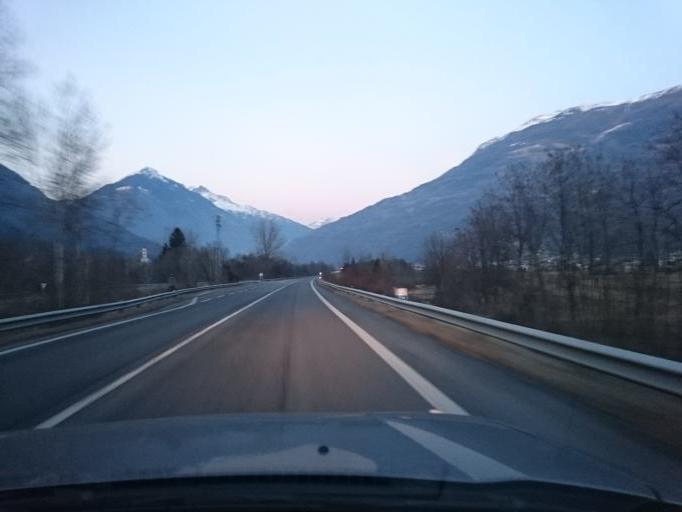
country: IT
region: Lombardy
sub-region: Provincia di Sondrio
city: Vervio
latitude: 46.2509
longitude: 10.2429
